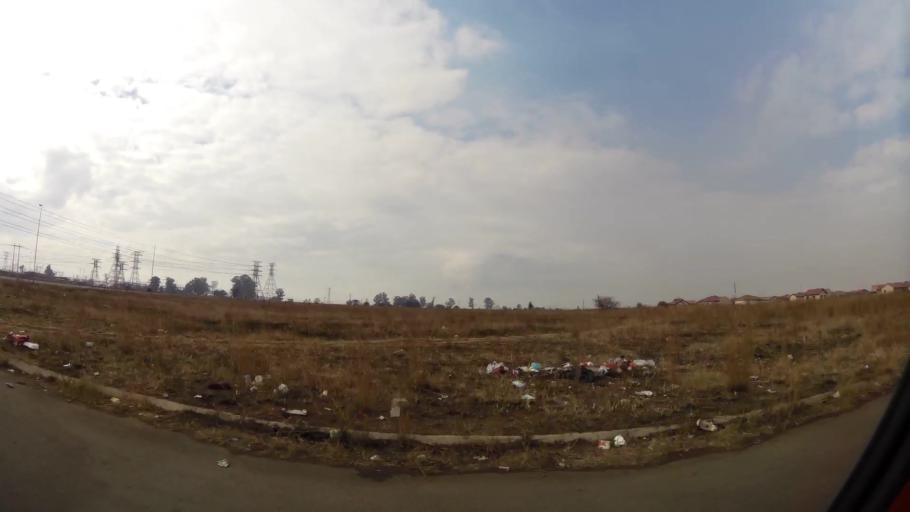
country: ZA
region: Gauteng
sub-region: Sedibeng District Municipality
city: Vanderbijlpark
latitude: -26.6811
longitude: 27.8496
